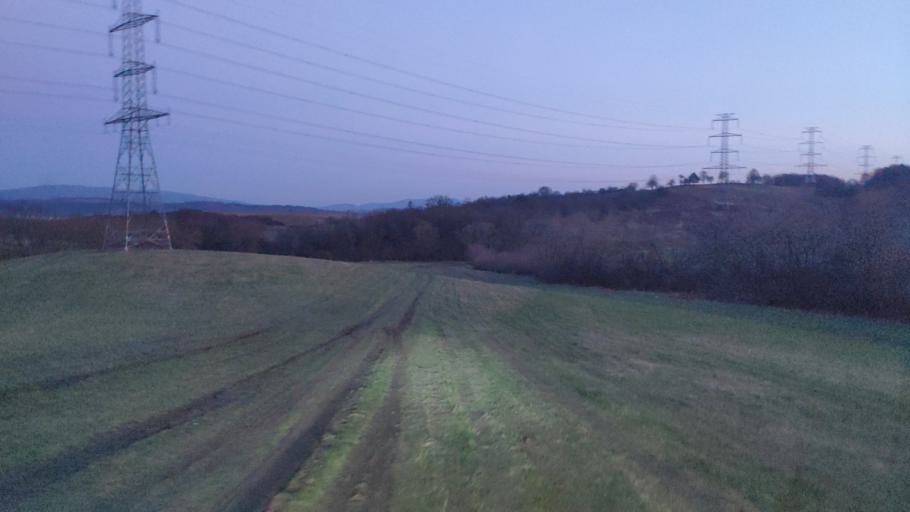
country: SK
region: Kosicky
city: Kosice
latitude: 48.8230
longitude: 21.2687
